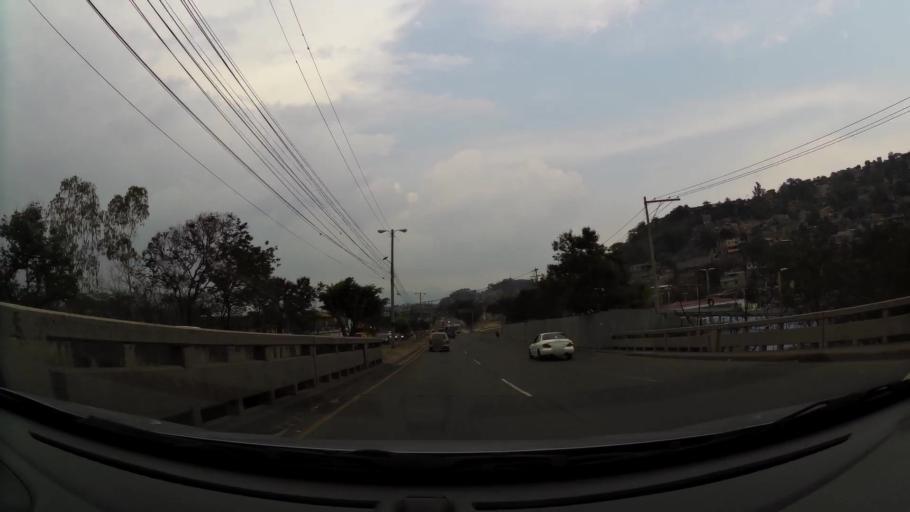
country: HN
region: Francisco Morazan
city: Tegucigalpa
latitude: 14.0865
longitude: -87.2290
